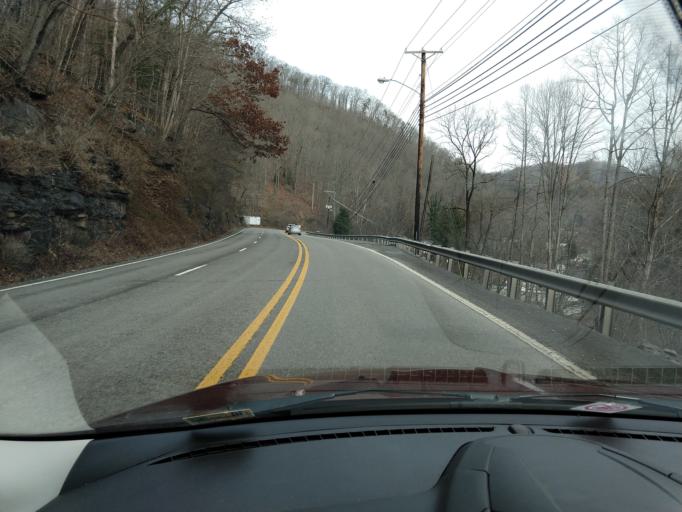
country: US
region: West Virginia
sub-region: McDowell County
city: Welch
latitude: 37.4139
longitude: -81.6020
